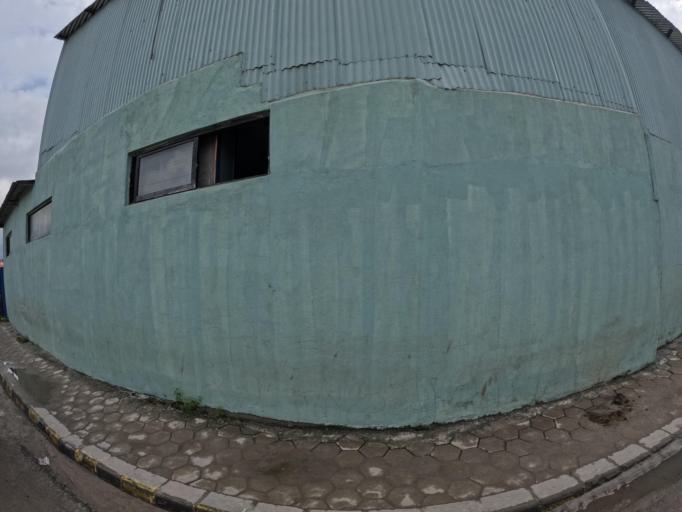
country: NP
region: Central Region
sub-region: Bagmati Zone
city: Kathmandu
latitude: 27.7520
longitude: 85.3163
